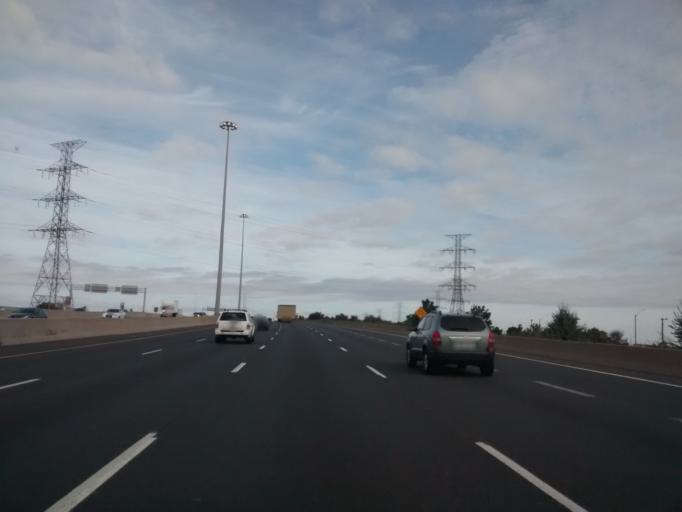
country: CA
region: Ontario
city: Hamilton
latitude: 43.2612
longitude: -79.7698
